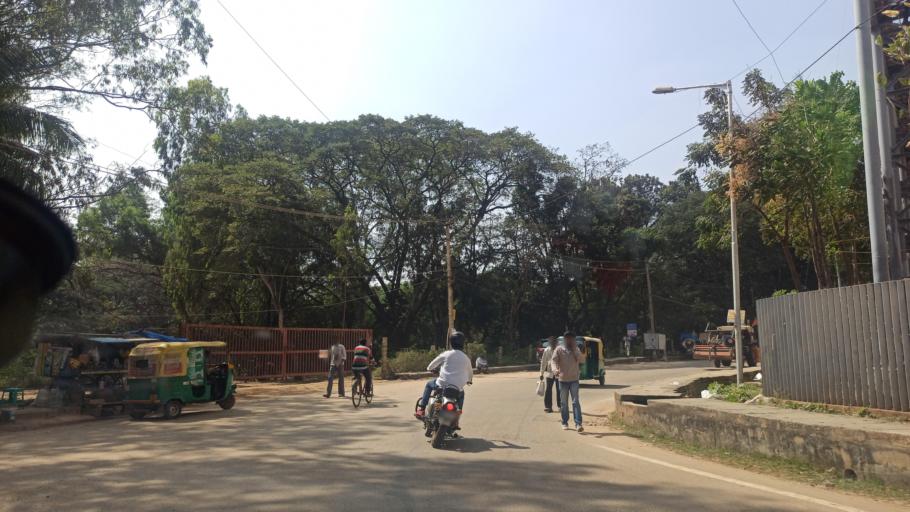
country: IN
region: Karnataka
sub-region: Bangalore Urban
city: Yelahanka
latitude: 13.0495
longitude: 77.5953
